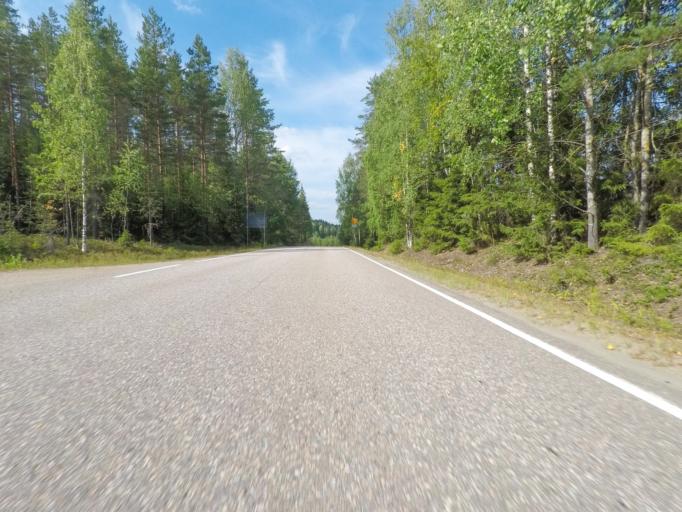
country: FI
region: Southern Savonia
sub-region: Savonlinna
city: Sulkava
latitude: 61.7232
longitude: 28.2056
